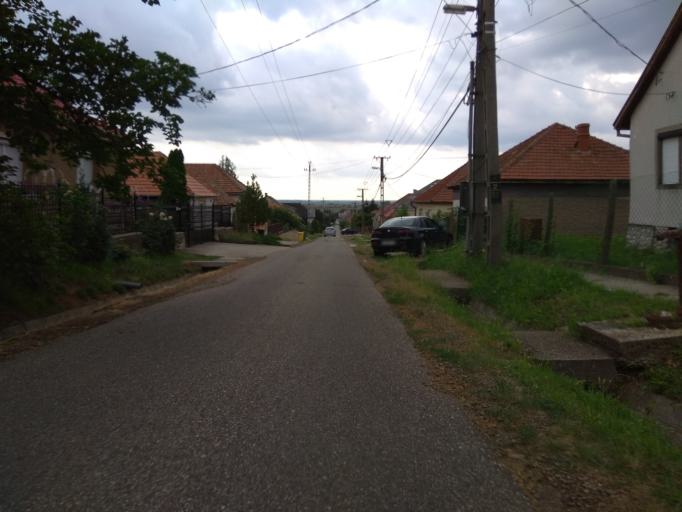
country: HU
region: Borsod-Abauj-Zemplen
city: Bekecs
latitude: 48.1540
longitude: 21.1627
